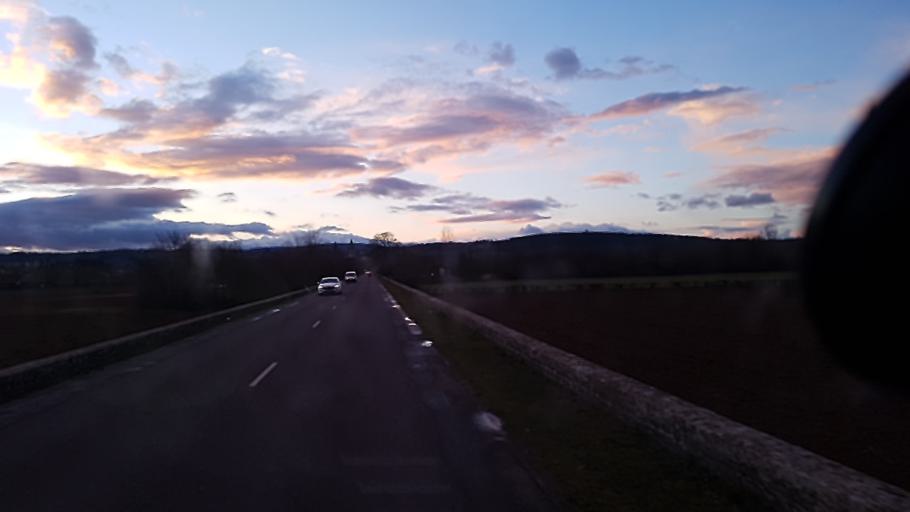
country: FR
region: Bourgogne
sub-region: Departement de Saone-et-Loire
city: Tournus
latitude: 46.5616
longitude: 4.9251
